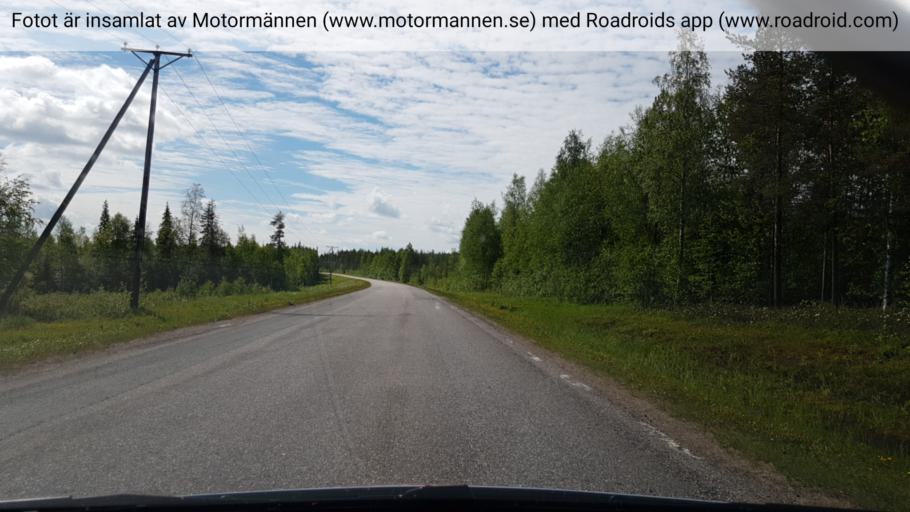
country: FI
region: Lapland
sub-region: Torniolaakso
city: Pello
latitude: 66.6338
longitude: 23.8629
